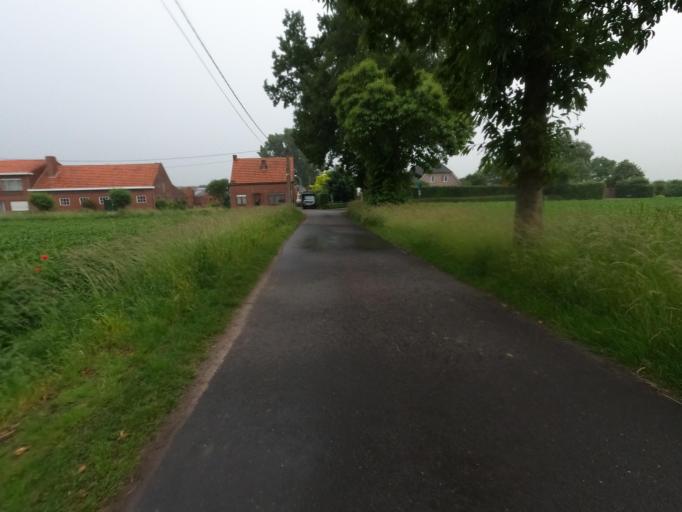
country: BE
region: Flanders
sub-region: Provincie Antwerpen
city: Kalmthout
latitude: 51.4248
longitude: 4.5194
